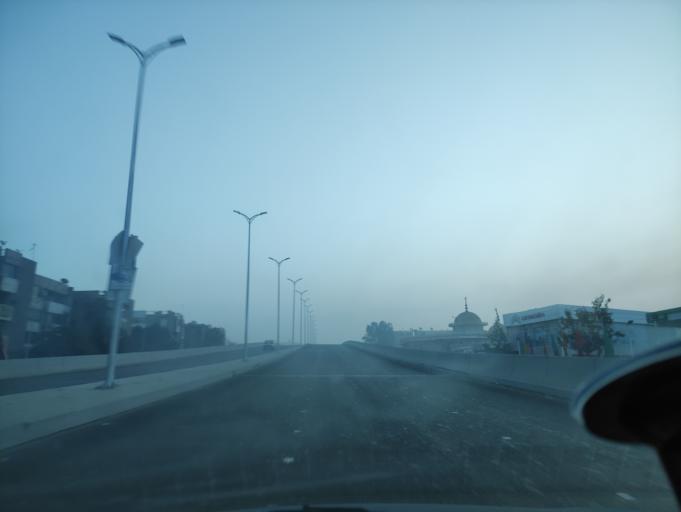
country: EG
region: Muhafazat al Qahirah
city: Cairo
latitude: 30.0463
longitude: 31.3543
